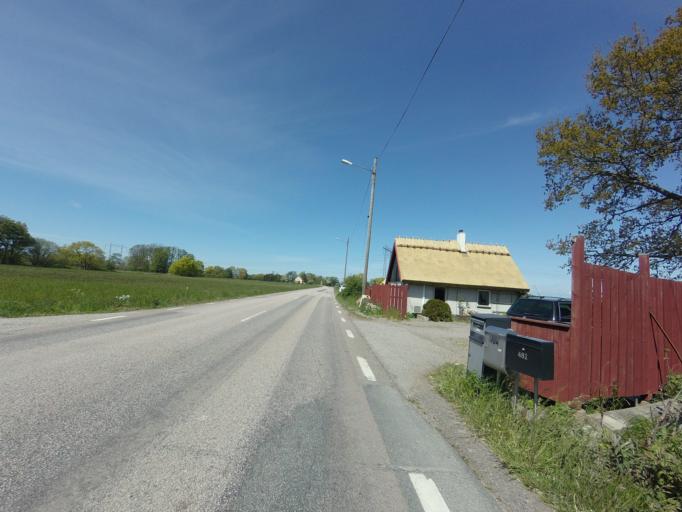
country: SE
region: Skane
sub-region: Helsingborg
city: Odakra
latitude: 56.1346
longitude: 12.6910
